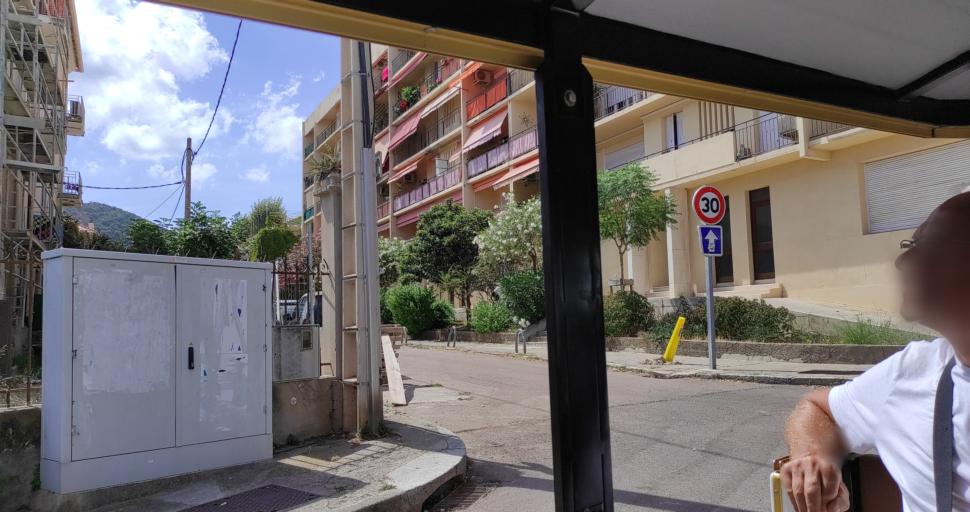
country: FR
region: Corsica
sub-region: Departement de la Corse-du-Sud
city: Ajaccio
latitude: 41.9160
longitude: 8.7265
